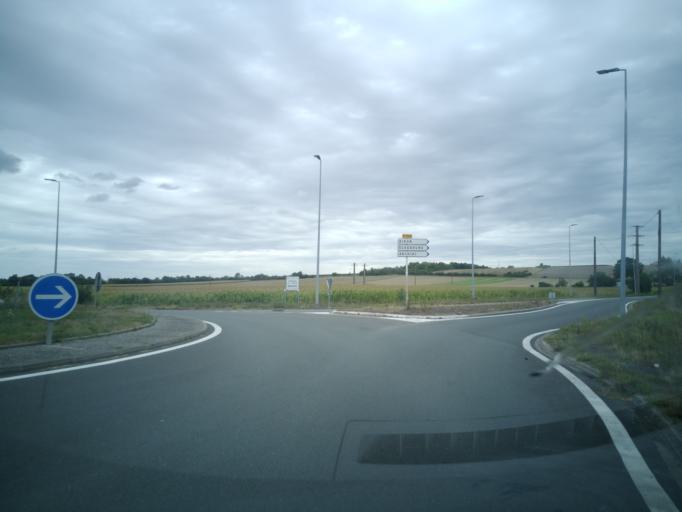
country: FR
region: Poitou-Charentes
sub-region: Departement de la Charente-Maritime
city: Pons
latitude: 45.5794
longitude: -0.5270
